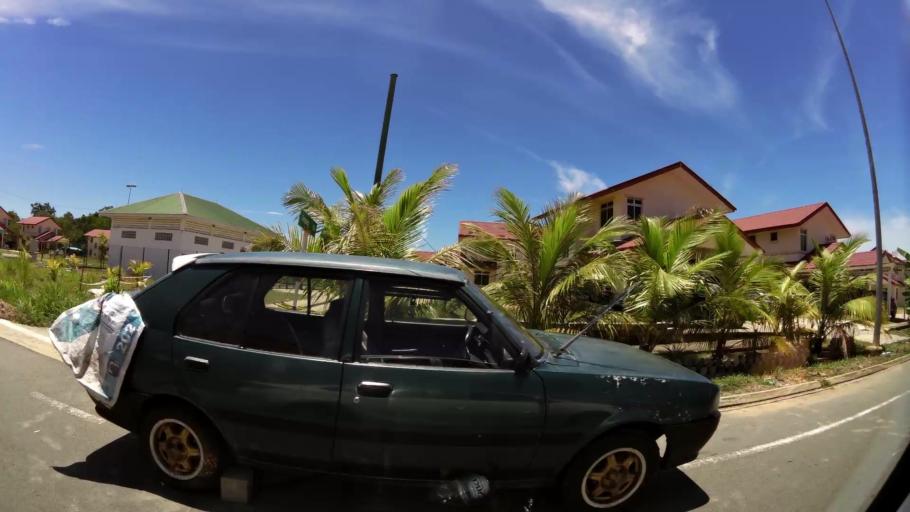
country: BN
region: Brunei and Muara
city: Bandar Seri Begawan
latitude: 5.0196
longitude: 115.0311
